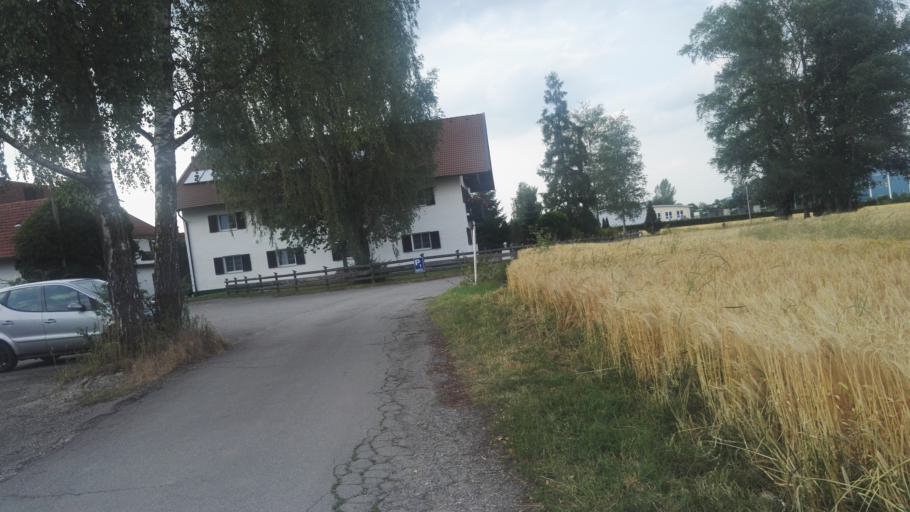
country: DE
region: Bavaria
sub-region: Upper Bavaria
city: Freilassing
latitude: 47.8403
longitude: 12.9639
